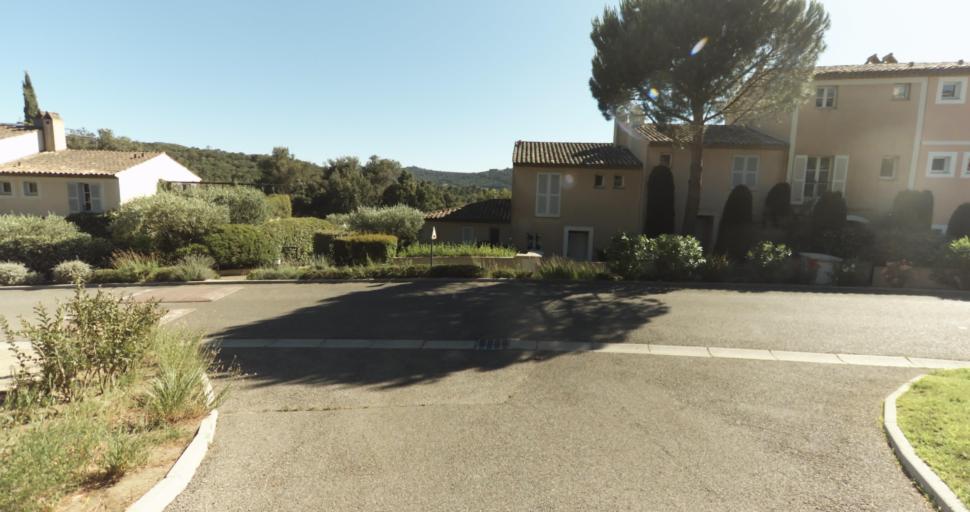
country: FR
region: Provence-Alpes-Cote d'Azur
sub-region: Departement du Var
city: Gassin
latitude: 43.2539
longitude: 6.6038
